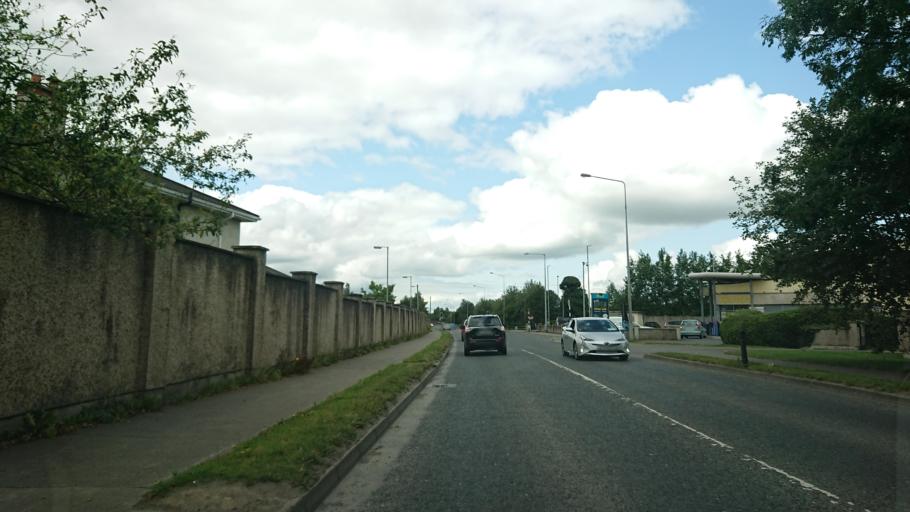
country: IE
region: Leinster
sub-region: Kildare
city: Johnstown
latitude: 53.2356
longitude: -6.6446
